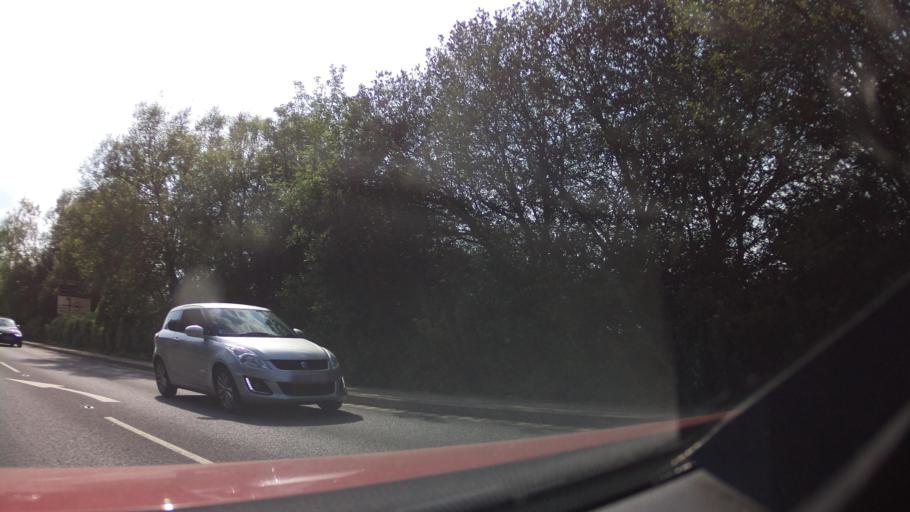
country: GB
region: England
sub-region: Wiltshire
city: Leigh
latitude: 51.6692
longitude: -1.9048
